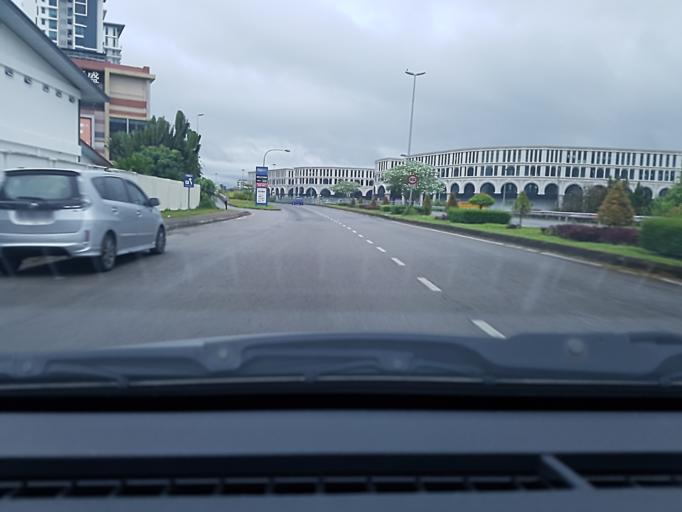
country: MY
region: Sarawak
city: Kuching
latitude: 1.5268
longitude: 110.3723
